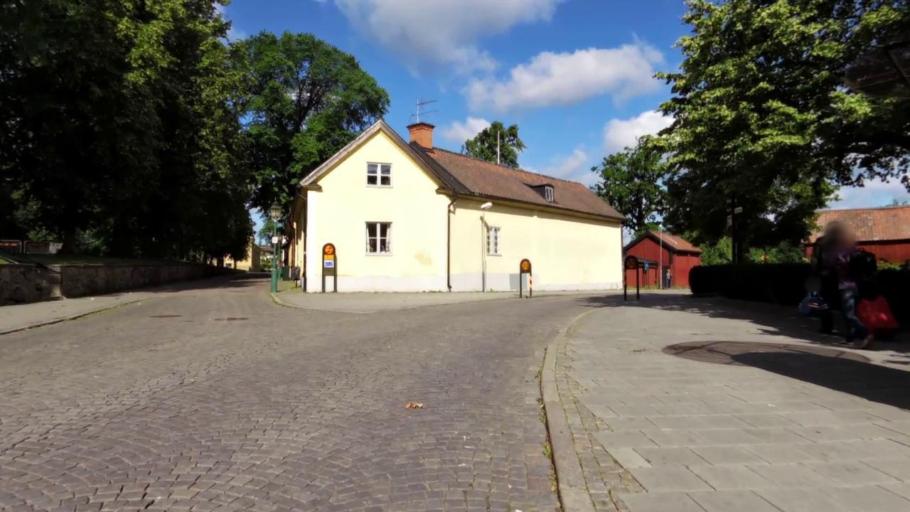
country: SE
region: OEstergoetland
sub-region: Linkopings Kommun
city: Linkoping
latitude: 58.4117
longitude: 15.6188
